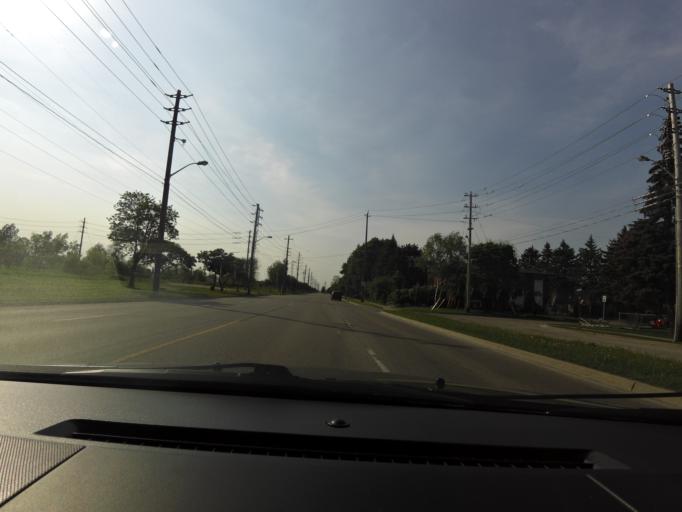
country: CA
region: Ontario
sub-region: Wellington County
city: Guelph
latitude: 43.5542
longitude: -80.2816
